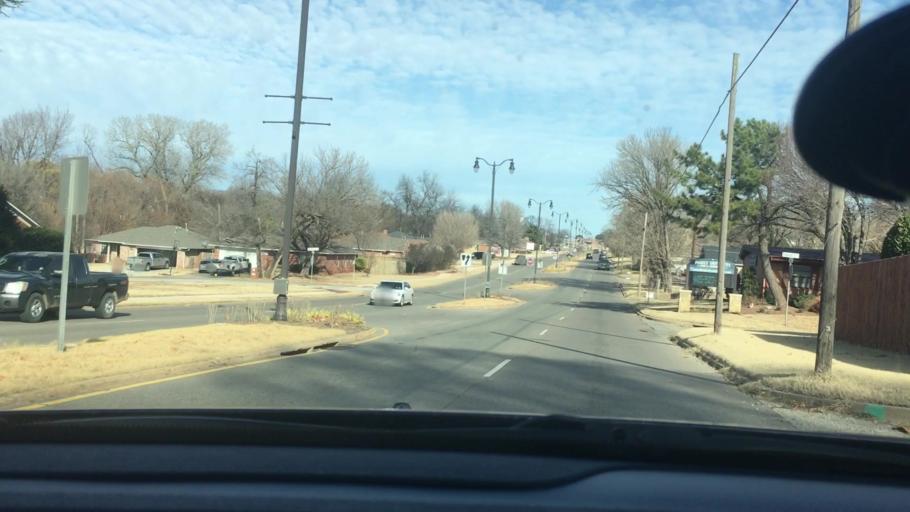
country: US
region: Oklahoma
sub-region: McClain County
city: Purcell
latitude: 35.0171
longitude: -97.3658
